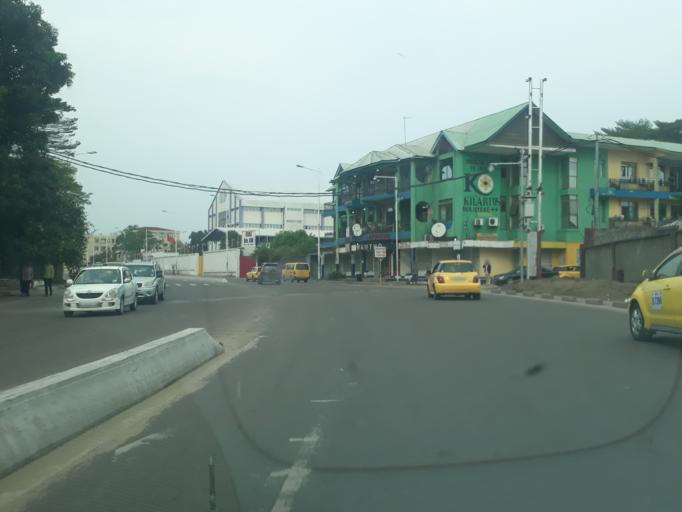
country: CD
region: Kinshasa
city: Kinshasa
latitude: -4.3332
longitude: 15.2615
